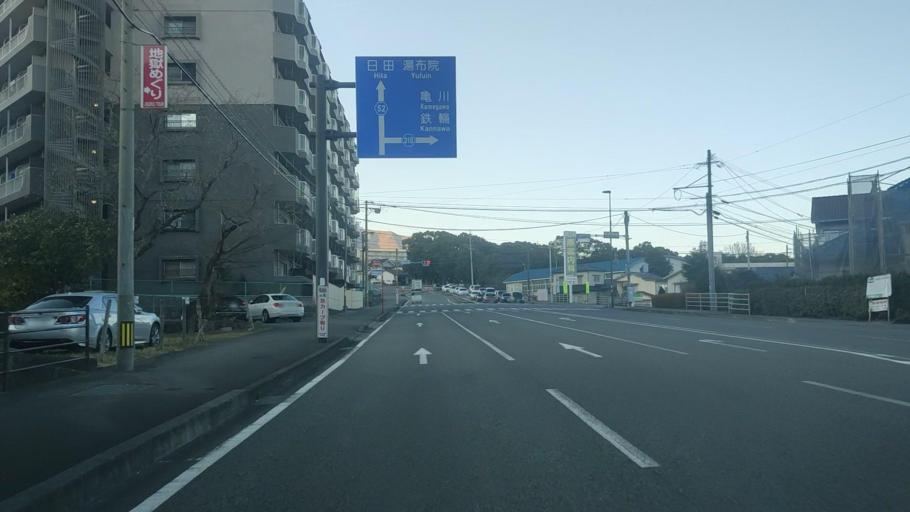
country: JP
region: Oita
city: Beppu
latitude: 33.2872
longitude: 131.4733
